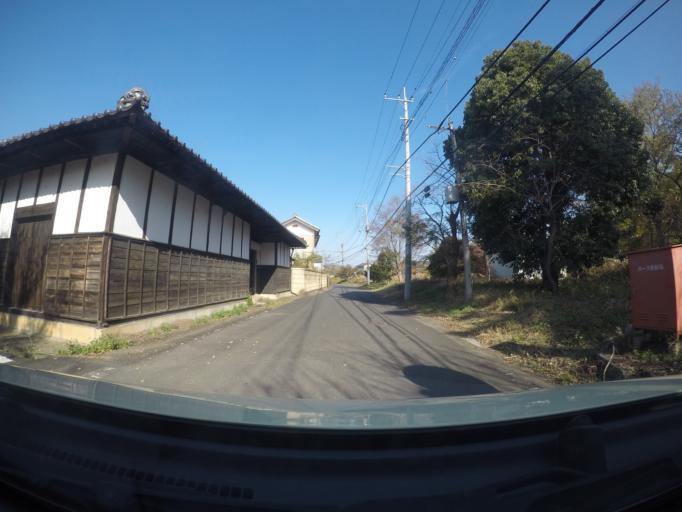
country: JP
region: Ibaraki
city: Naka
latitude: 36.0931
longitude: 140.1151
